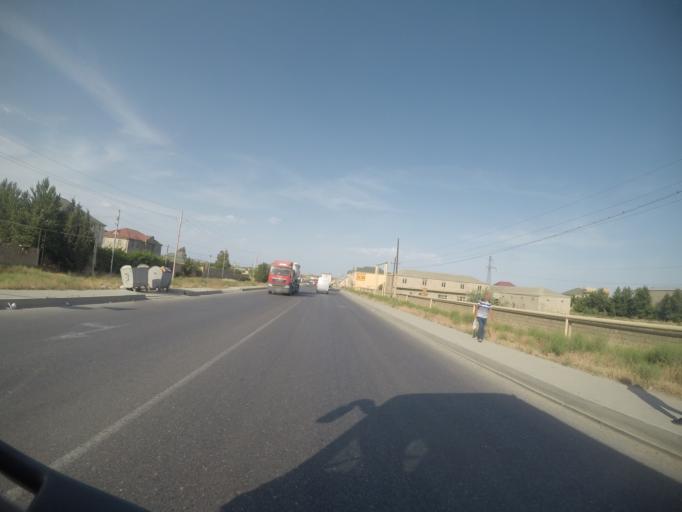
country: AZ
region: Baki
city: Bilajari
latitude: 40.4455
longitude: 49.7944
